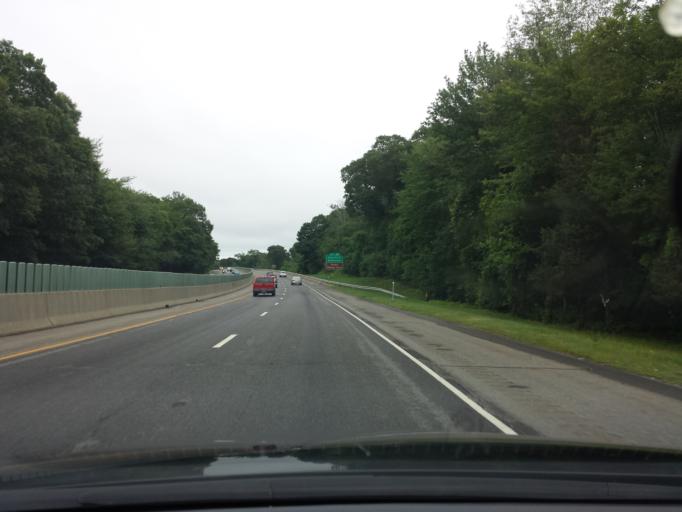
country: US
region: Connecticut
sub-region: Middlesex County
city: Old Saybrook
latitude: 41.3082
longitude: -72.3711
